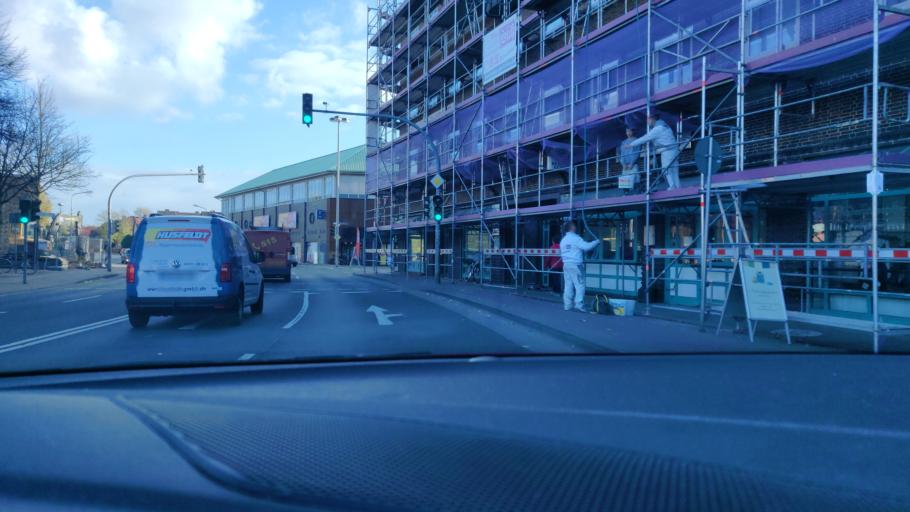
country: DE
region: Lower Saxony
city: Cuxhaven
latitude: 53.8613
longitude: 8.7022
